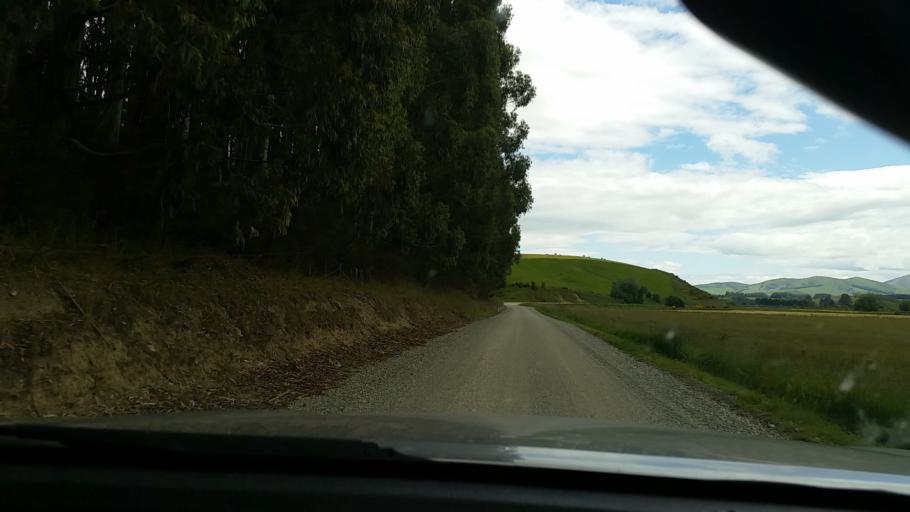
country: NZ
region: Otago
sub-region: Queenstown-Lakes District
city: Kingston
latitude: -45.7579
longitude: 168.6044
